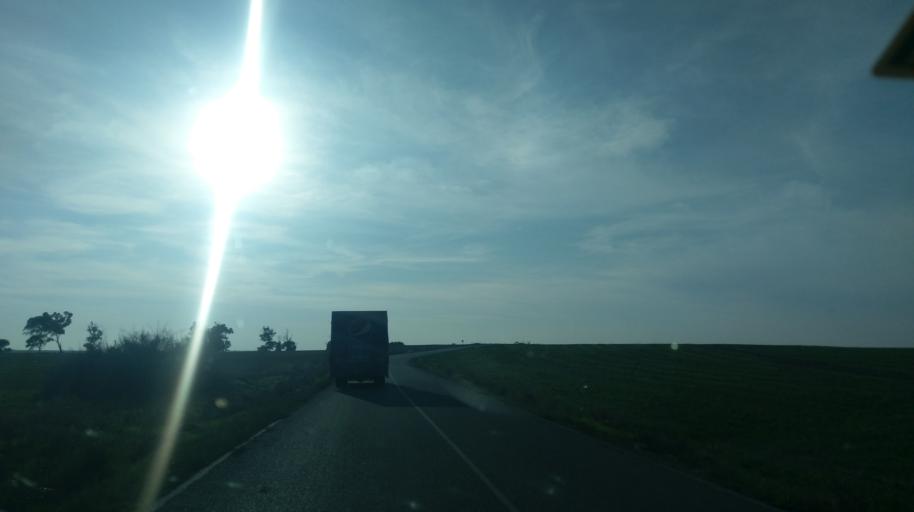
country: CY
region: Ammochostos
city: Acheritou
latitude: 35.0959
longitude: 33.8436
